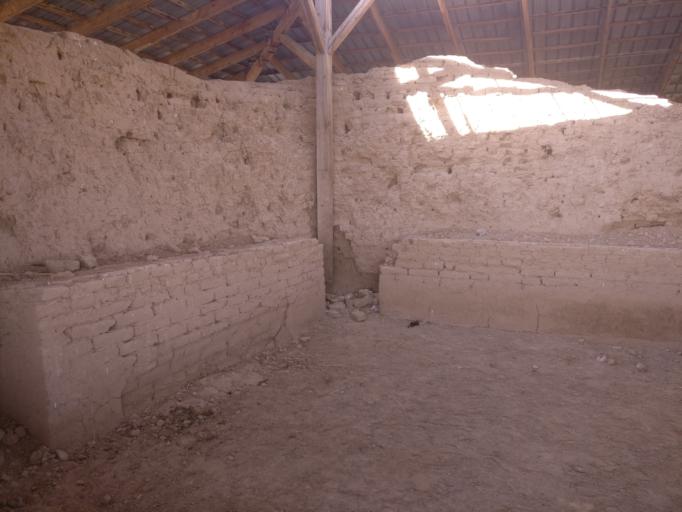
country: KG
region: Chuy
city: Ivanovka
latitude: 42.9086
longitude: 75.0175
